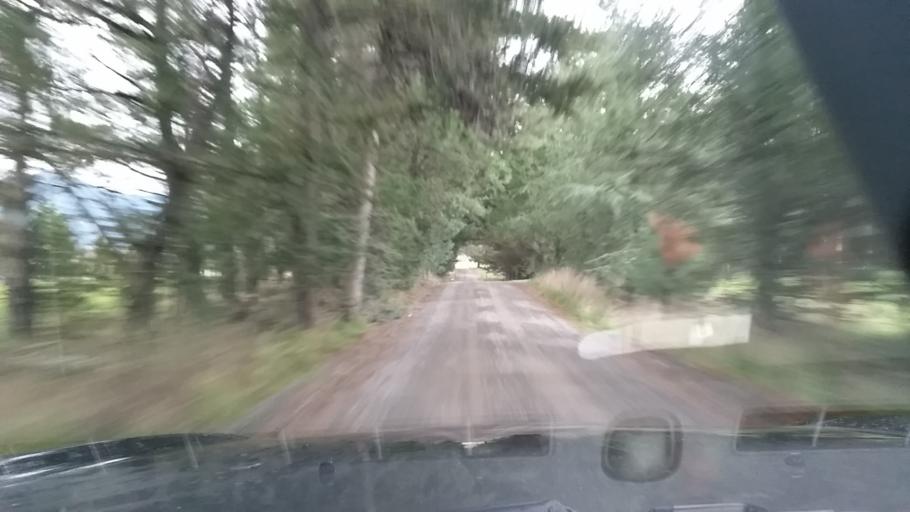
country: NZ
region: Marlborough
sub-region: Marlborough District
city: Blenheim
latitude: -41.5379
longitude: 173.6150
